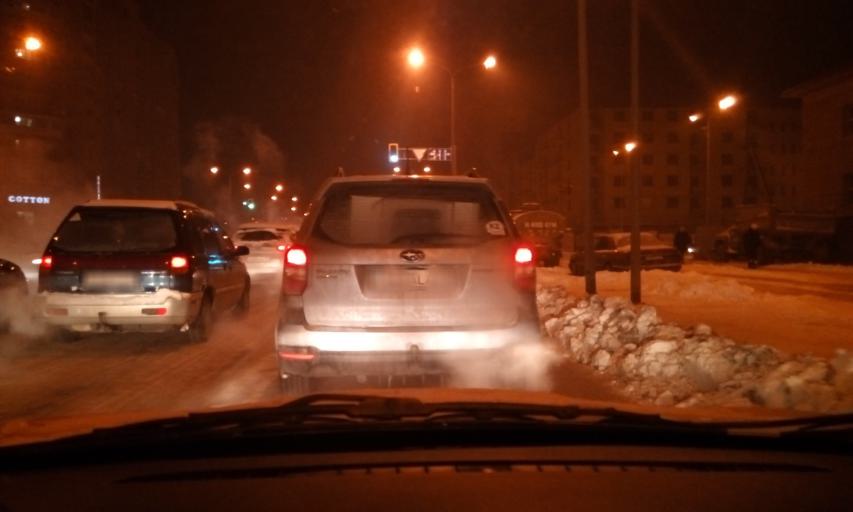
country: KZ
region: Astana Qalasy
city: Astana
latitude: 51.1320
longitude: 71.4951
